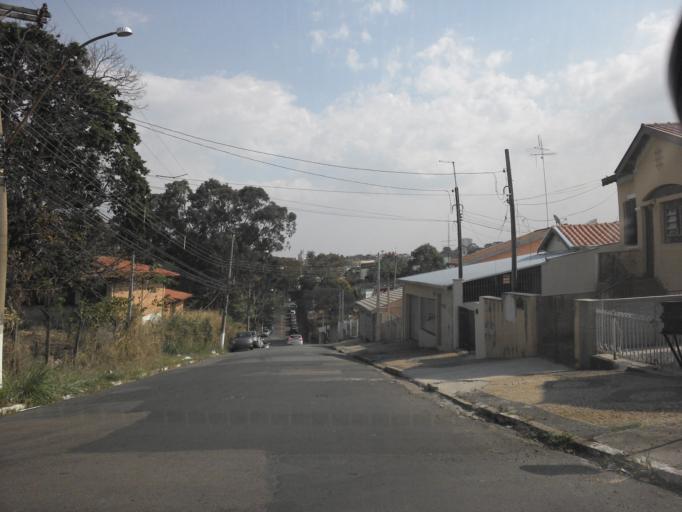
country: BR
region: Sao Paulo
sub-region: Campinas
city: Campinas
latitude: -22.9123
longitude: -47.0674
